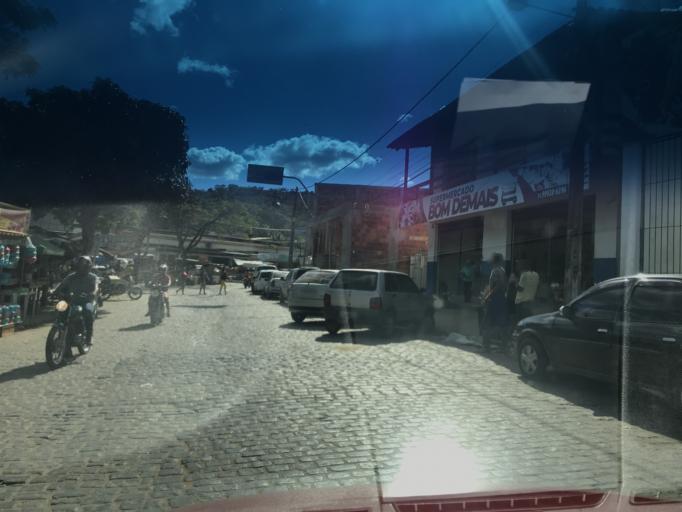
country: BR
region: Bahia
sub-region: Gandu
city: Gandu
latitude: -13.7441
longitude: -39.4887
